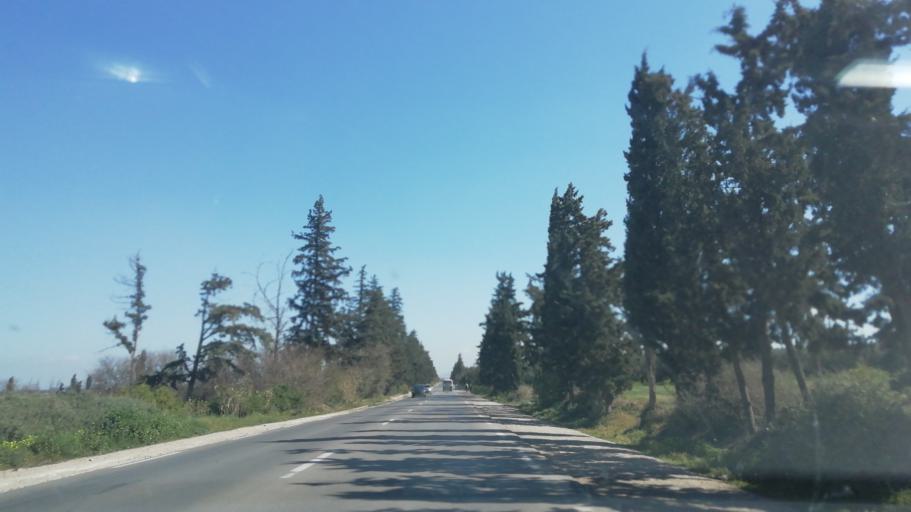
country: DZ
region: Mascara
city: Sig
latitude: 35.5671
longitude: -0.0688
